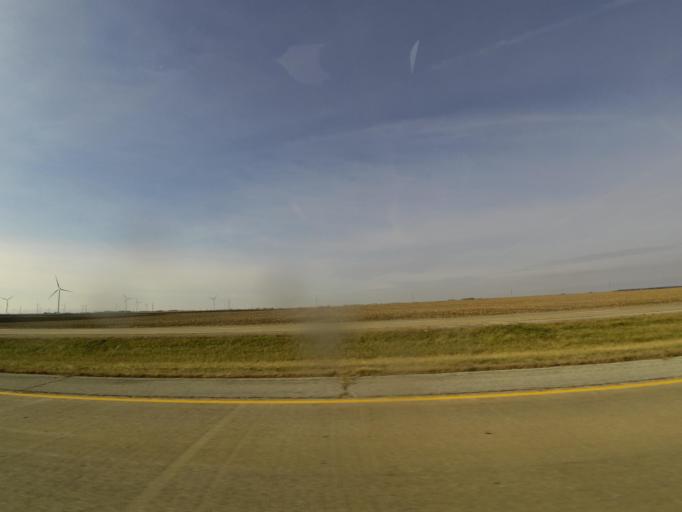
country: US
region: Illinois
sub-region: Macon County
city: Maroa
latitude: 40.0601
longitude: -88.9656
